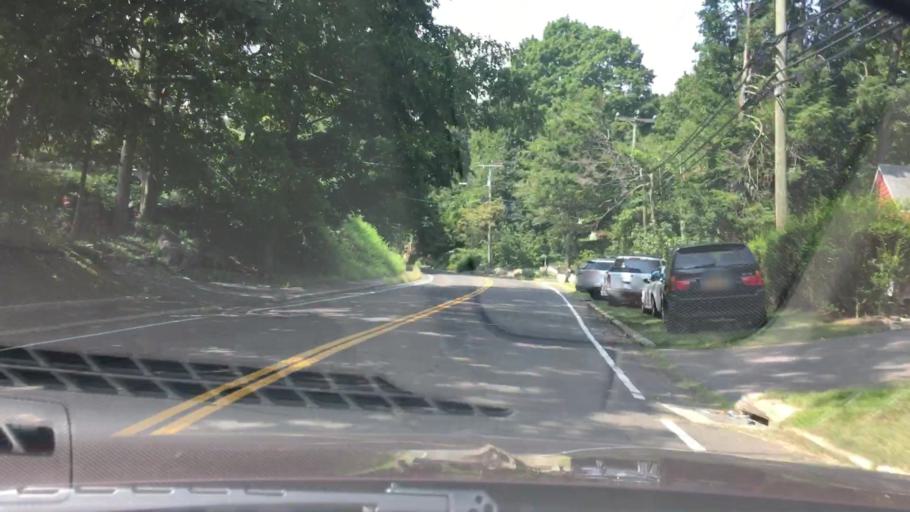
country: US
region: Connecticut
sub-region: Fairfield County
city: Norwalk
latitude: 41.1282
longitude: -73.4122
